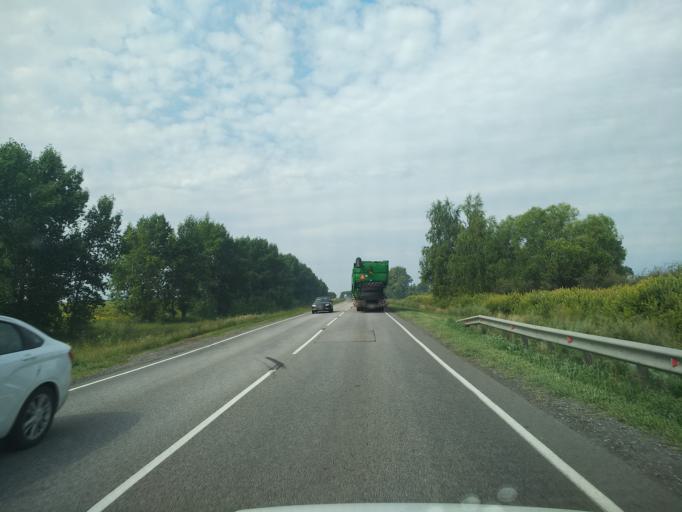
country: RU
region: Voronezj
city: Pereleshinskiy
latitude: 51.8724
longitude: 40.3947
